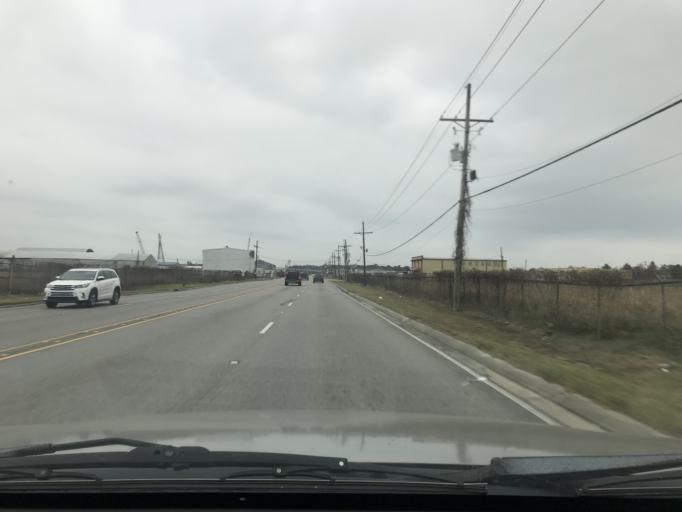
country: US
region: Louisiana
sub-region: Jefferson Parish
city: Woodmere
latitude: 29.8799
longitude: -90.0753
